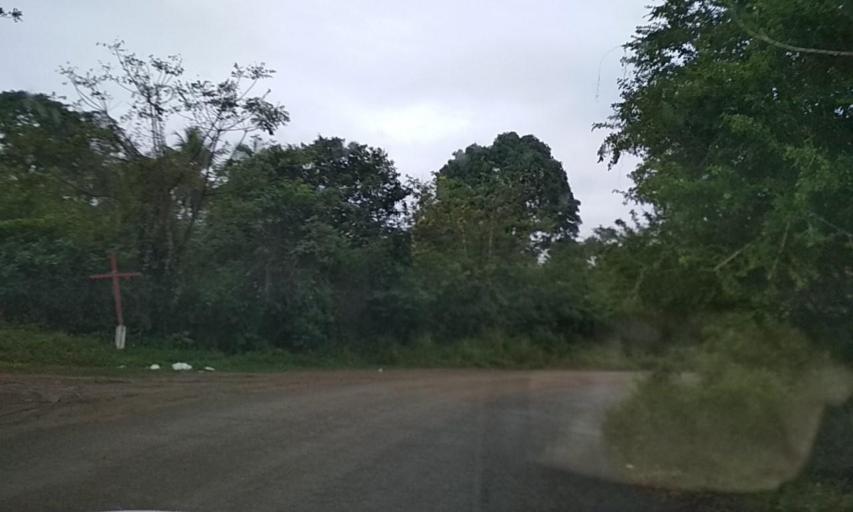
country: MX
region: Veracruz
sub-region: Coatzintla
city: Manuel Maria Contreras
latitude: 20.4491
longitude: -97.4782
